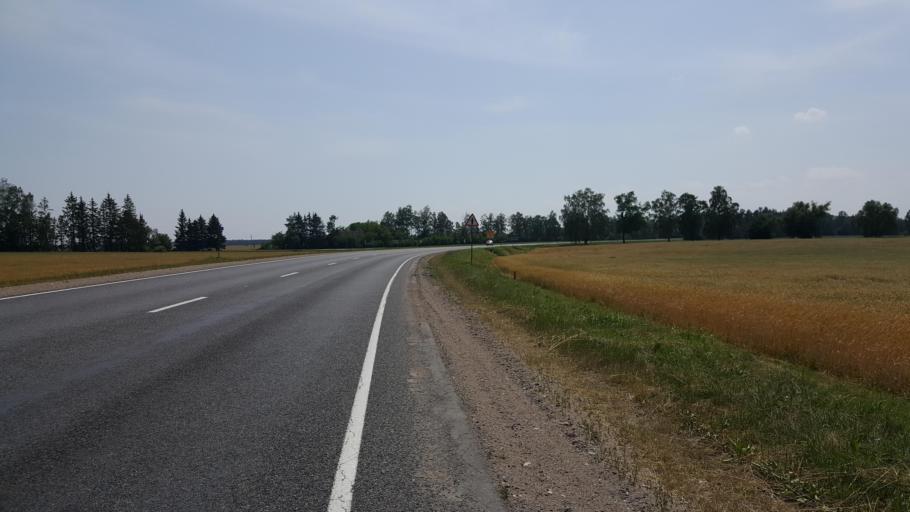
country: BY
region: Brest
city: Kamyanyets
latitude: 52.3728
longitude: 23.7922
